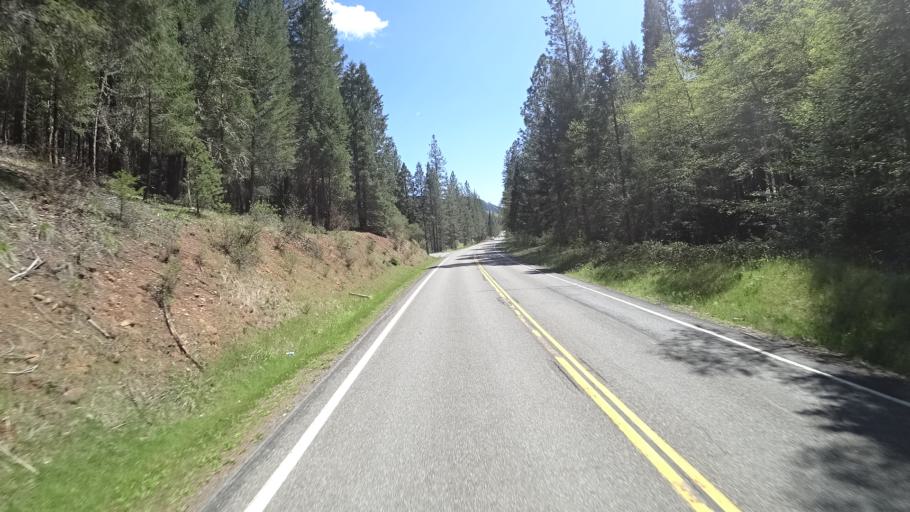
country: US
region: California
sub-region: Trinity County
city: Weaverville
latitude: 40.7625
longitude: -122.8876
